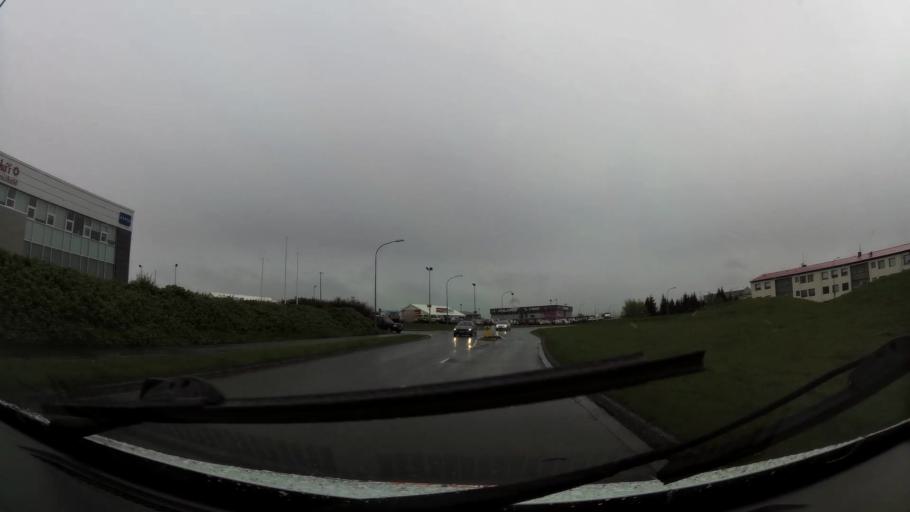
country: IS
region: Capital Region
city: Mosfellsbaer
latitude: 64.1167
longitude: -21.7861
